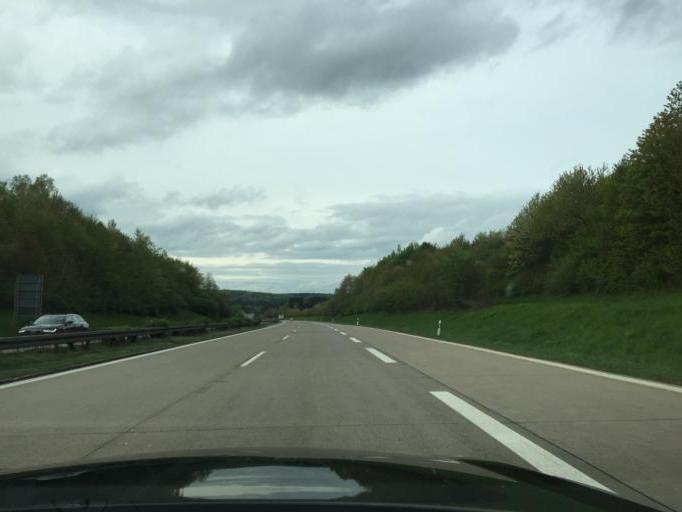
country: DE
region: Baden-Wuerttemberg
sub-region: Regierungsbezirk Stuttgart
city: Ellenberg
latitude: 48.9877
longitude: 10.1955
